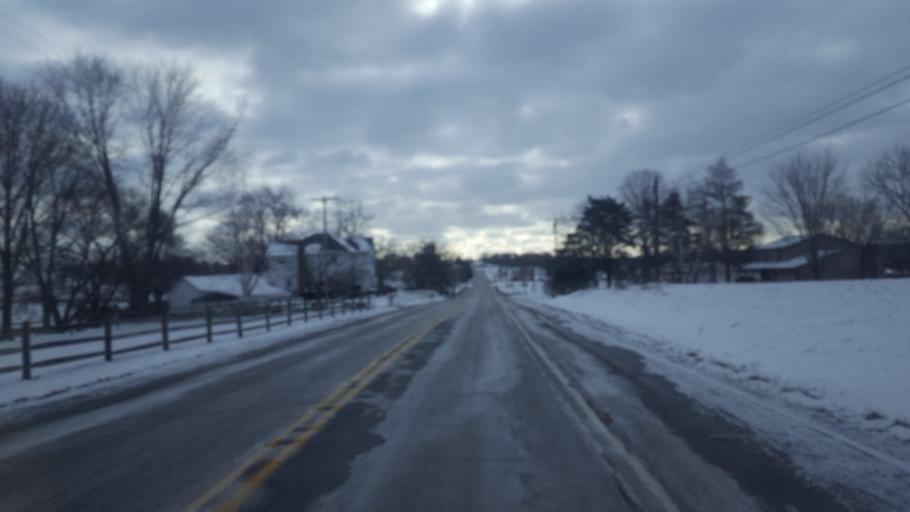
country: US
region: Pennsylvania
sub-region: Lawrence County
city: New Wilmington
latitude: 41.1195
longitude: -80.2871
